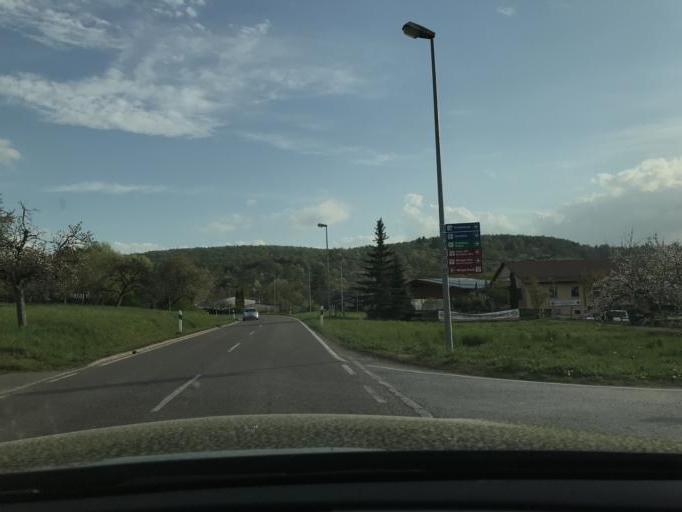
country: DE
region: Baden-Wuerttemberg
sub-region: Regierungsbezirk Stuttgart
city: Weinstadt-Endersbach
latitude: 48.7918
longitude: 9.3614
